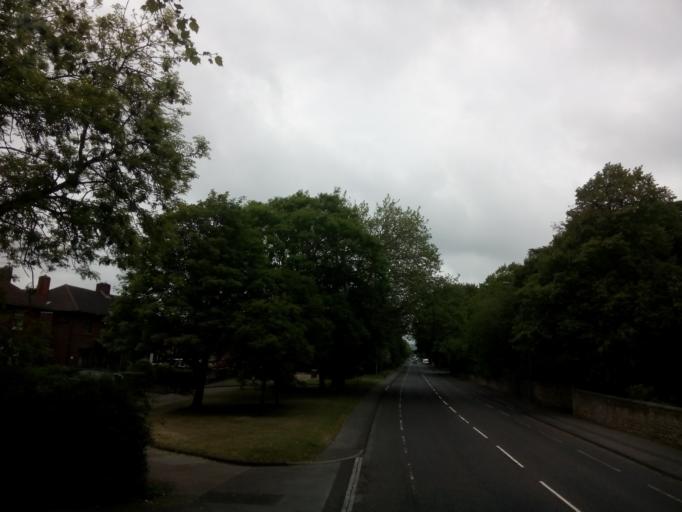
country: GB
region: England
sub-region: County Durham
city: Chester-le-Street
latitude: 54.8707
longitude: -1.5750
